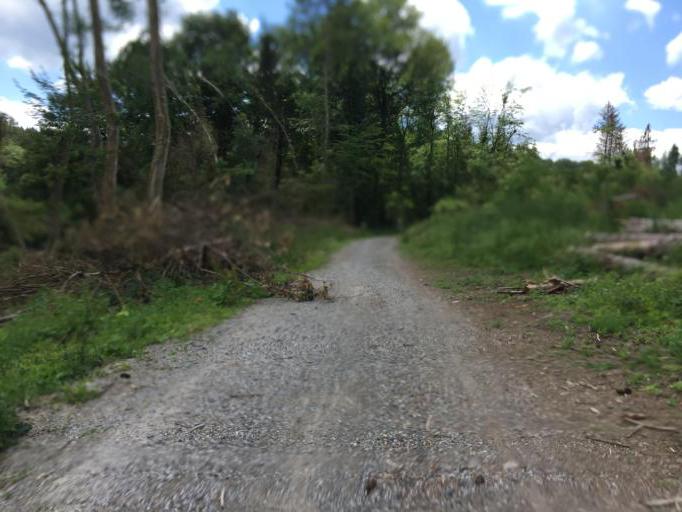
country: DE
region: Rheinland-Pfalz
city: Holler
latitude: 50.4236
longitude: 7.8569
